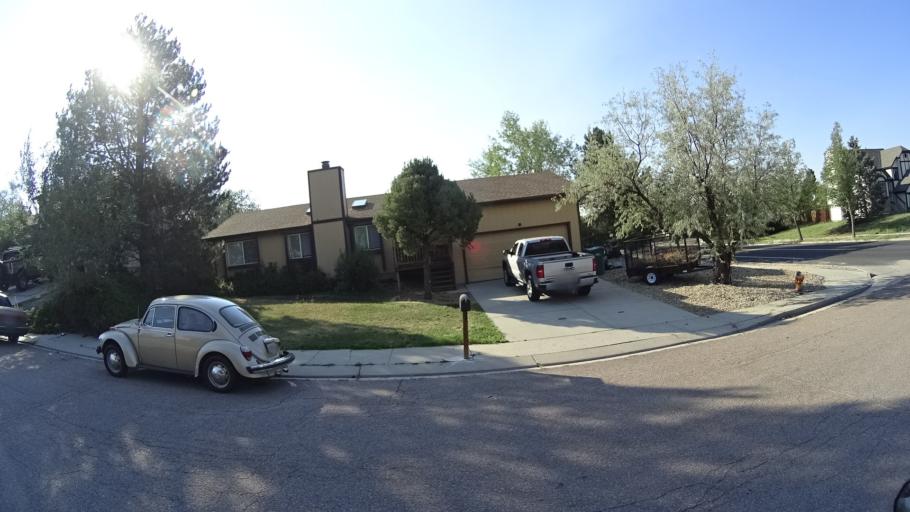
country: US
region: Colorado
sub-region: El Paso County
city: Stratmoor
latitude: 38.7783
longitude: -104.8040
